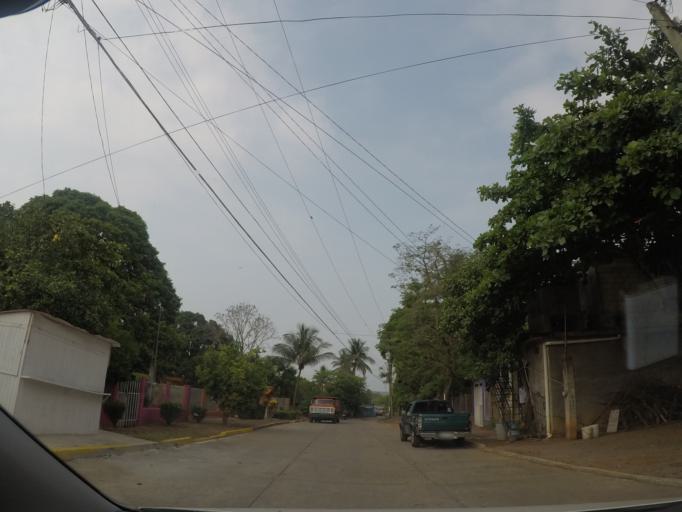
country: MX
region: Oaxaca
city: Colonia Rincon Viejo
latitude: 16.8811
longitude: -95.0461
